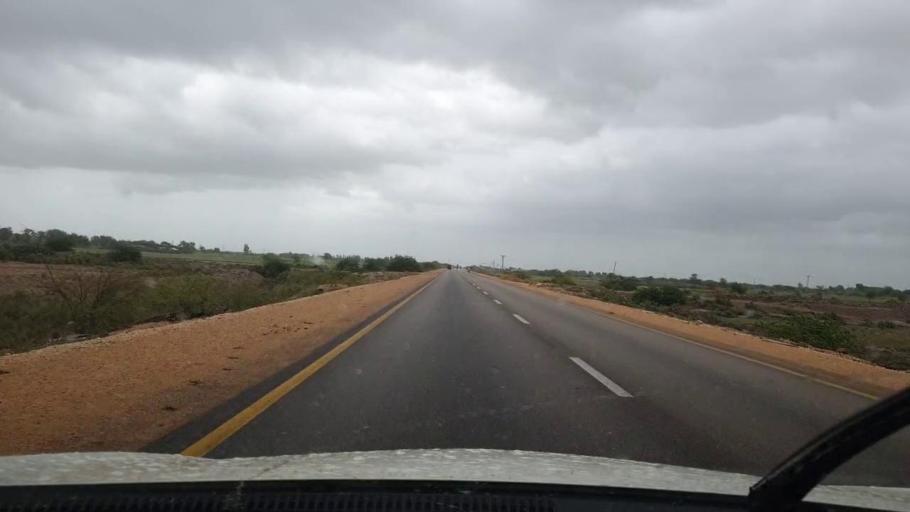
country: PK
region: Sindh
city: Badin
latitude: 24.6562
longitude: 68.6906
